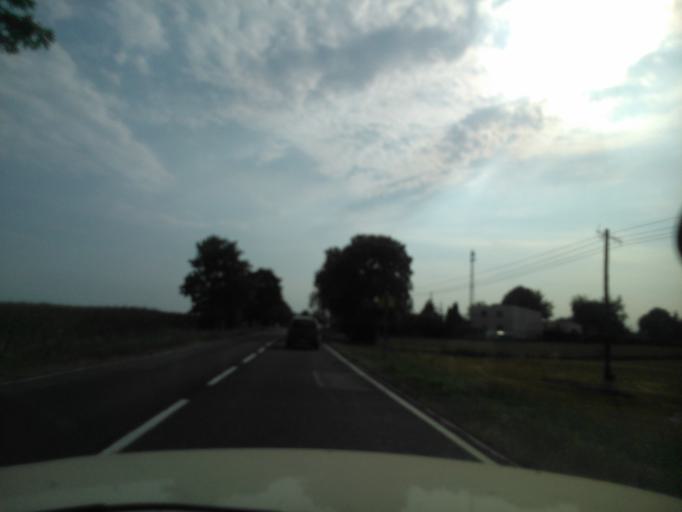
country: PL
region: Kujawsko-Pomorskie
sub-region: Powiat wabrzeski
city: Debowa Laka
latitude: 53.2107
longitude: 19.1755
